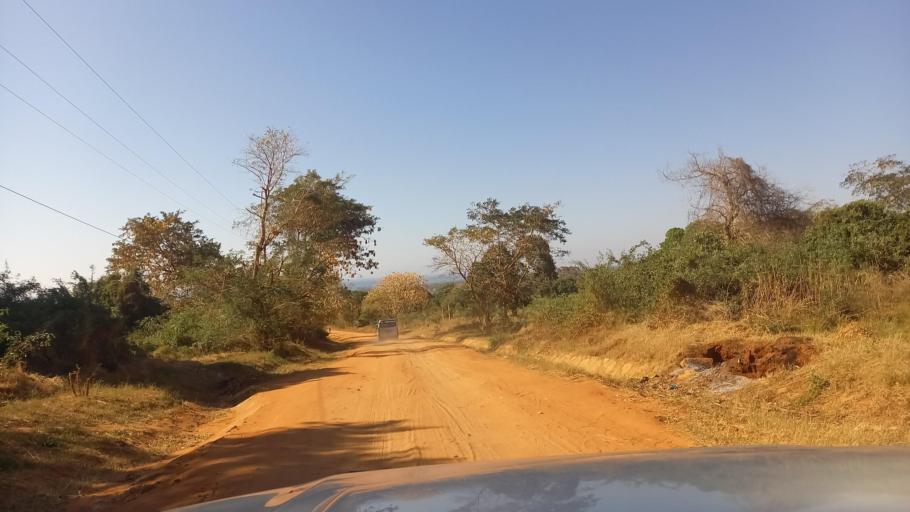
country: MZ
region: Cabo Delgado
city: Pemba
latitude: -13.0924
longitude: 40.5313
